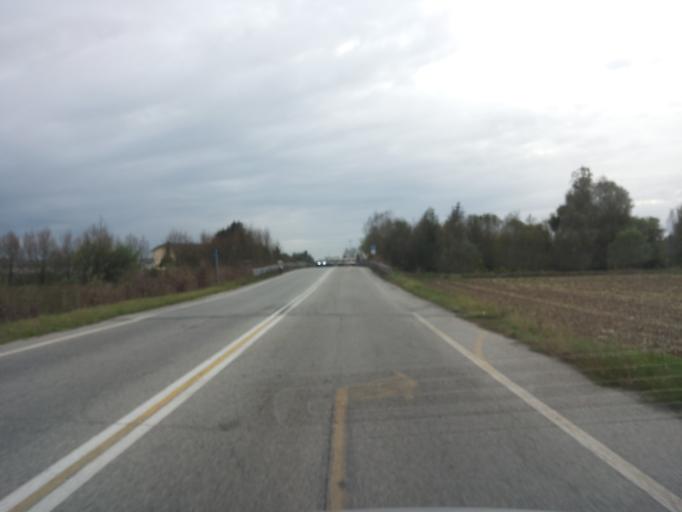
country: IT
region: Piedmont
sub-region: Provincia di Alessandria
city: Villanova Monferrato
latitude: 45.1763
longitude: 8.4718
